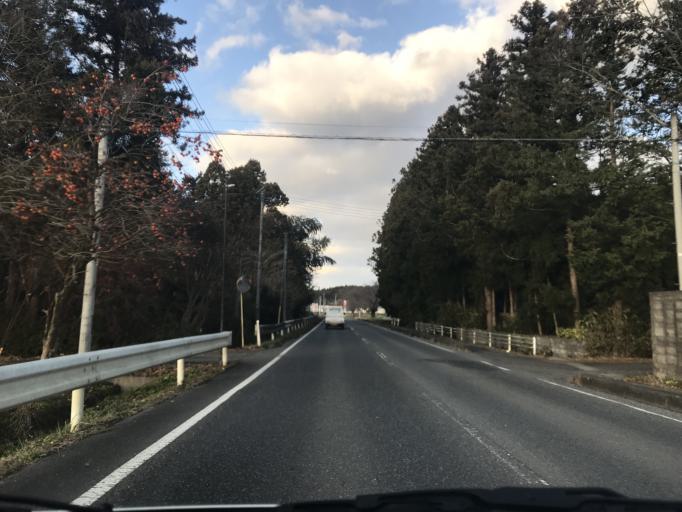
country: JP
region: Miyagi
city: Kogota
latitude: 38.6469
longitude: 141.0751
